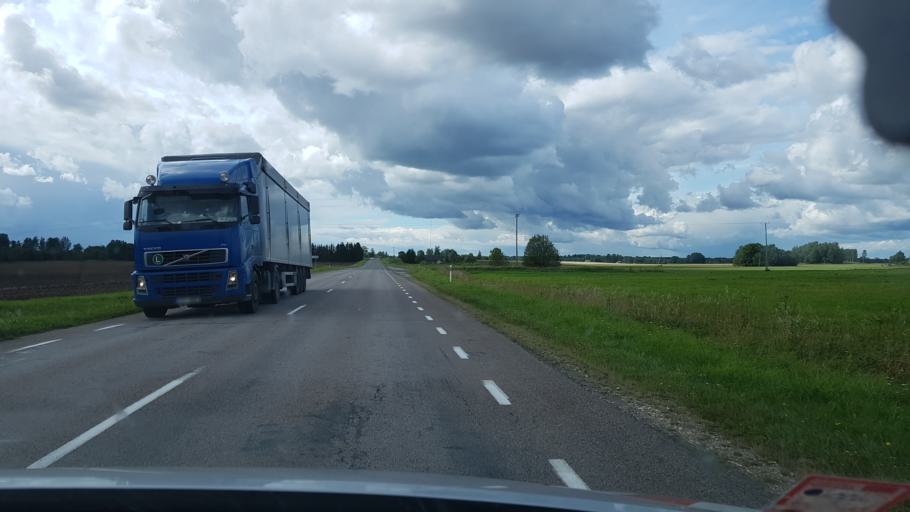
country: EE
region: Jaervamaa
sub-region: Jaerva-Jaani vald
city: Jarva-Jaani
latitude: 58.9202
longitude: 25.8796
